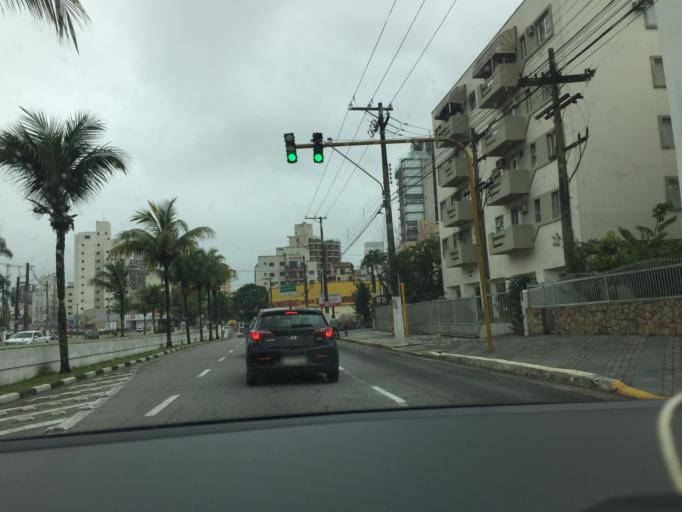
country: BR
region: Sao Paulo
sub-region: Guaruja
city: Guaruja
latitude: -23.9817
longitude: -46.2285
